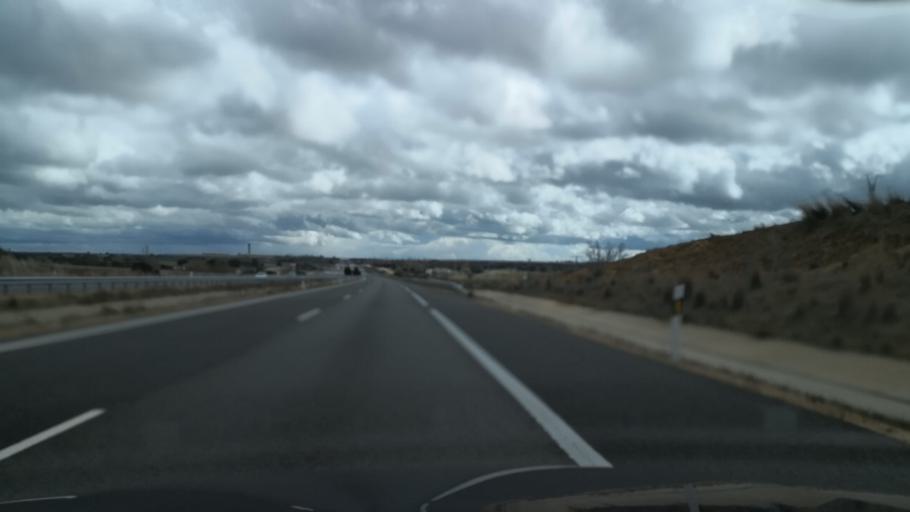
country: ES
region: Castille and Leon
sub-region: Provincia de Salamanca
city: Valdelosa
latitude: 41.2218
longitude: -5.7053
